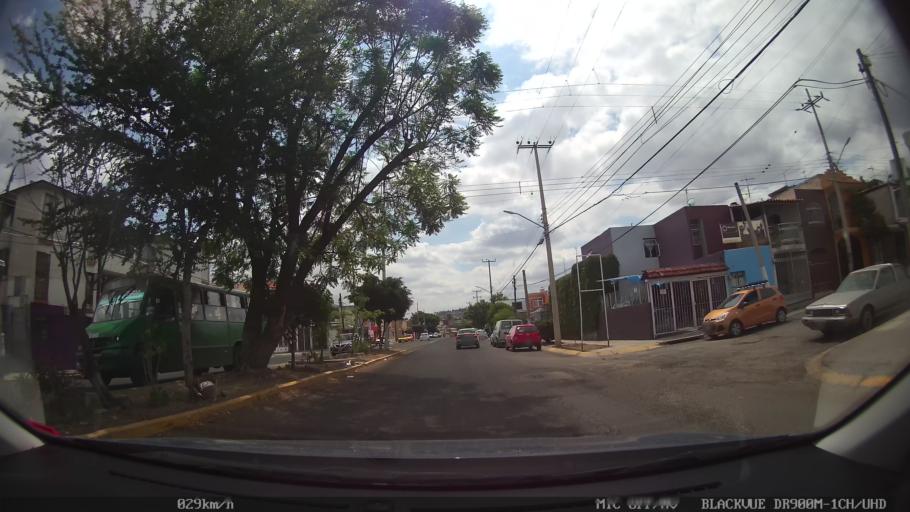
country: MX
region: Jalisco
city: Tonala
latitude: 20.6315
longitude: -103.2622
